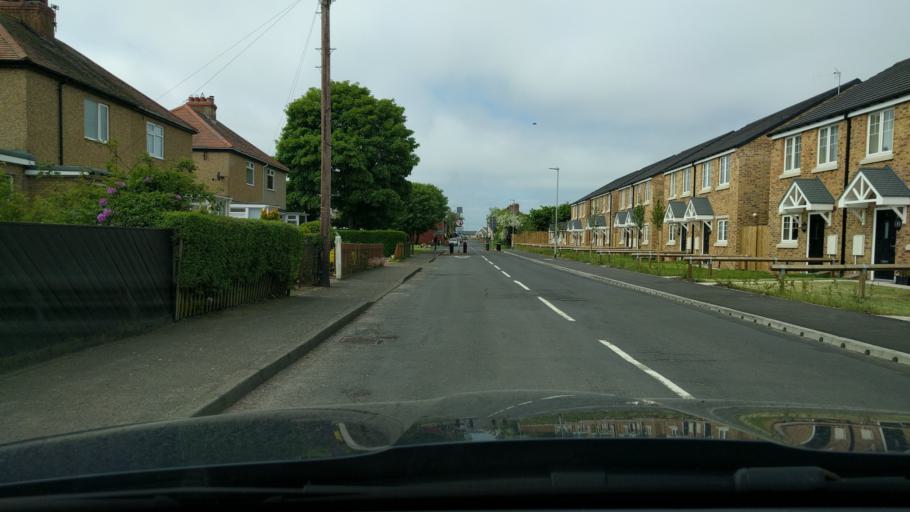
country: GB
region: England
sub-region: Northumberland
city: Acklington
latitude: 55.3084
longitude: -1.6103
